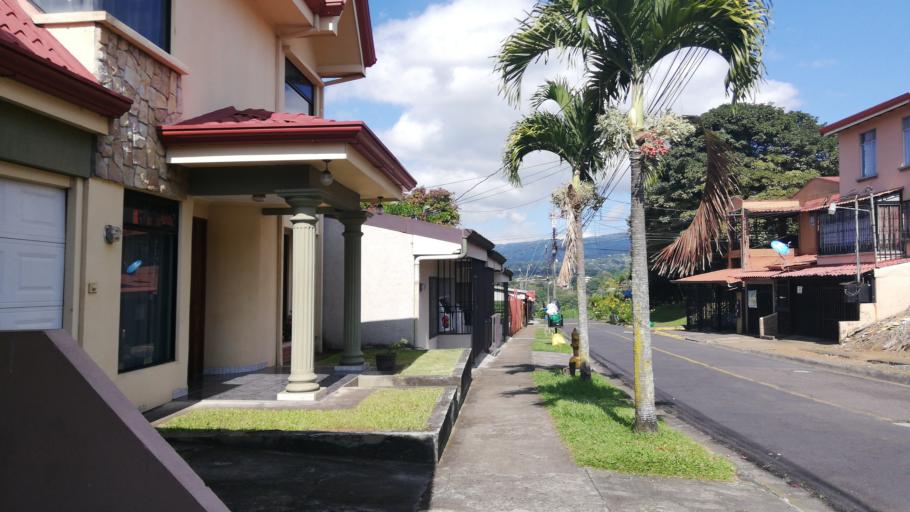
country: CR
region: Alajuela
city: San Juan
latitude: 10.0786
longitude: -84.3087
